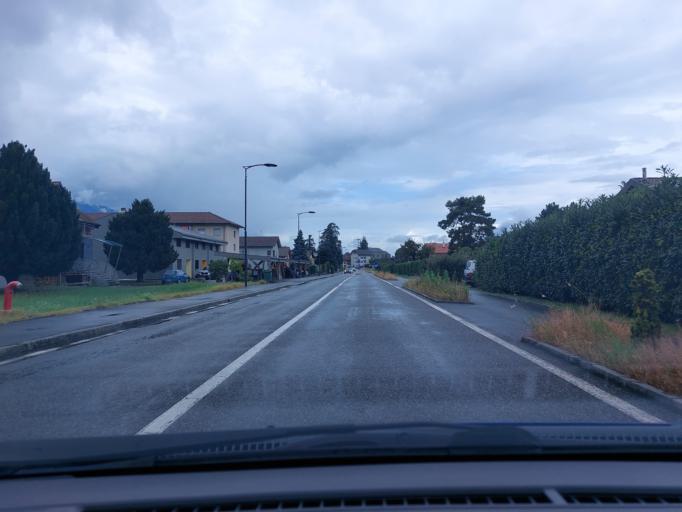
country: CH
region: Vaud
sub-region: Aigle District
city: Bex
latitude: 46.2395
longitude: 6.9918
